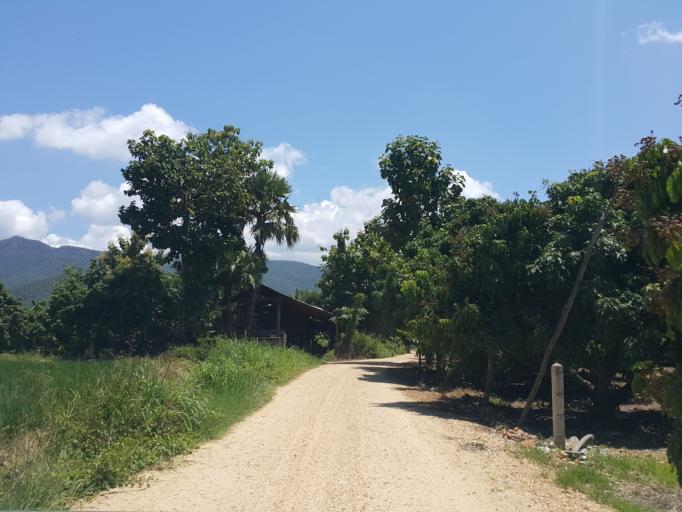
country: TH
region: Lamphun
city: Ban Thi
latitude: 18.6644
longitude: 99.1646
